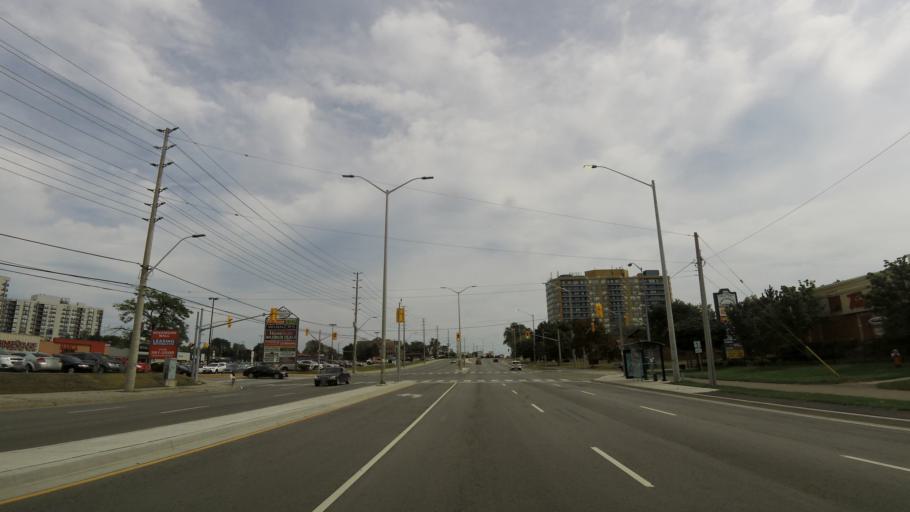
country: CA
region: Ontario
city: Etobicoke
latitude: 43.6248
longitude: -79.6058
